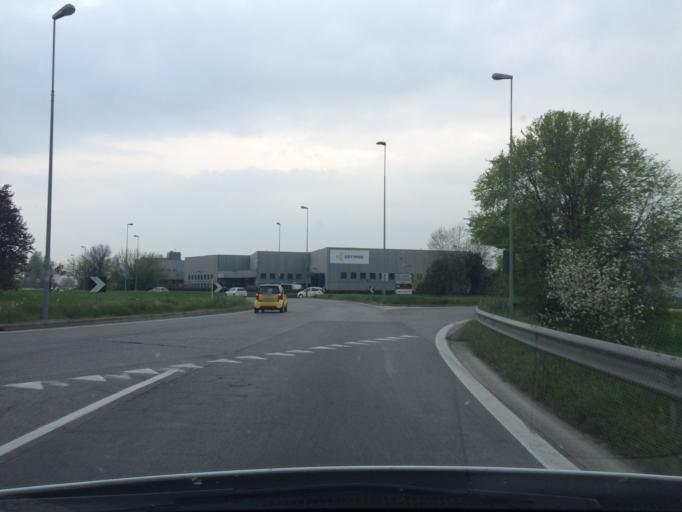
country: IT
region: Lombardy
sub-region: Provincia di Brescia
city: Roncadelle
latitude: 45.5085
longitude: 10.1664
